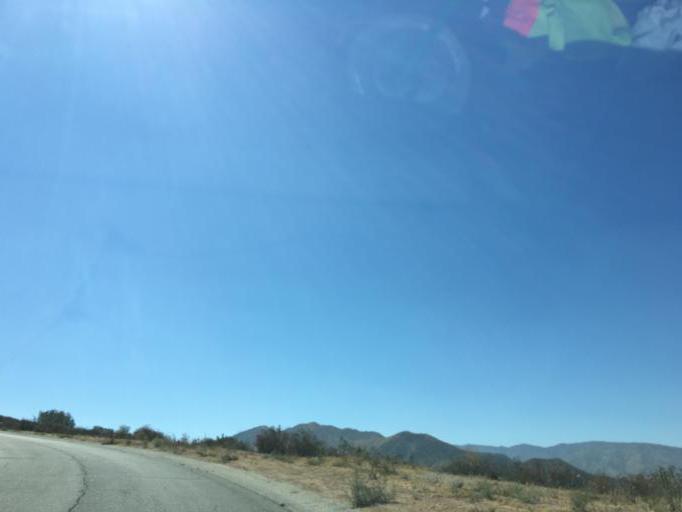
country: US
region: California
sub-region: Los Angeles County
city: Vincent
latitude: 34.4889
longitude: -118.1567
